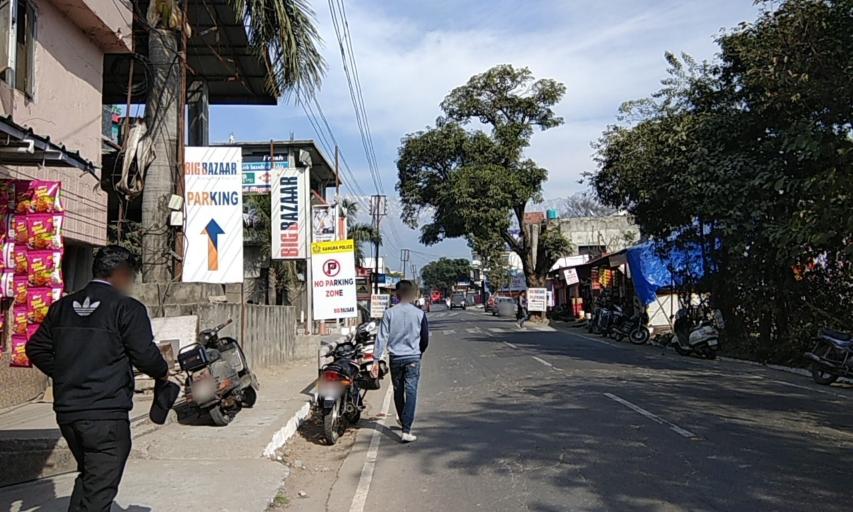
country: IN
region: Himachal Pradesh
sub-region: Kangra
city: Kangra
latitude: 32.1151
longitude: 76.2820
